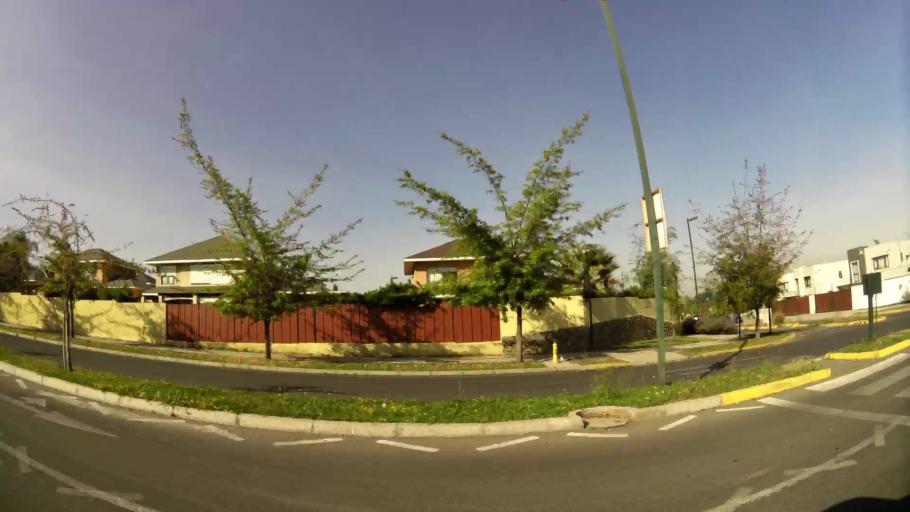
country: CL
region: Santiago Metropolitan
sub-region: Provincia de Santiago
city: Villa Presidente Frei, Nunoa, Santiago, Chile
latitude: -33.4931
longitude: -70.5548
